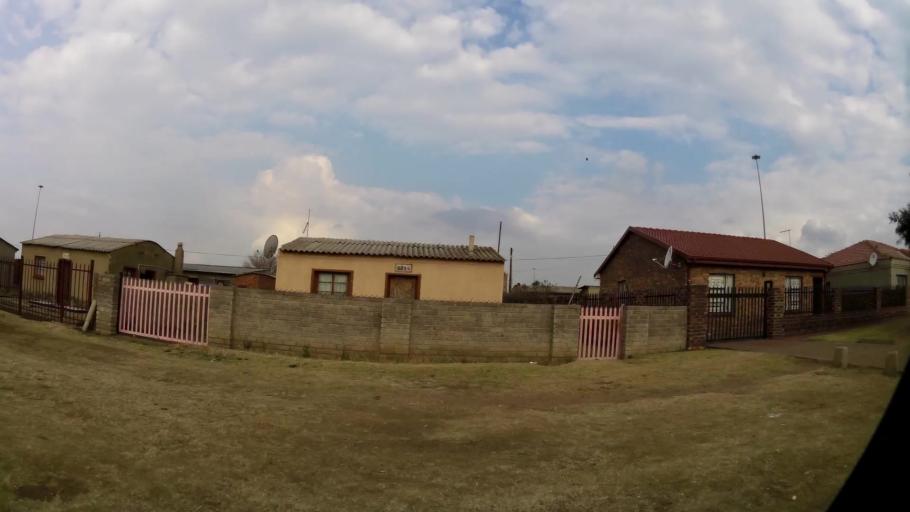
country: ZA
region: Gauteng
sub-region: Sedibeng District Municipality
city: Vereeniging
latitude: -26.6770
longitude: 27.8754
